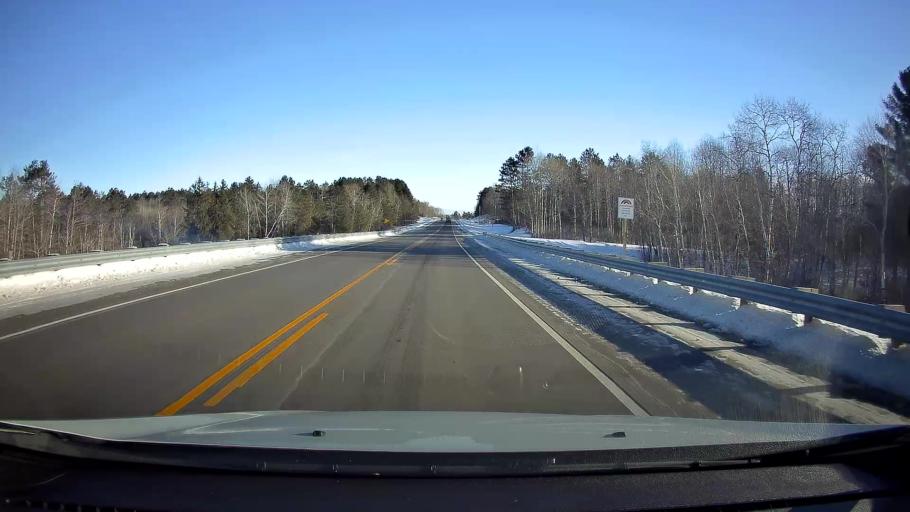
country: US
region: Wisconsin
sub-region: Sawyer County
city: Hayward
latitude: 46.0690
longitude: -91.4315
